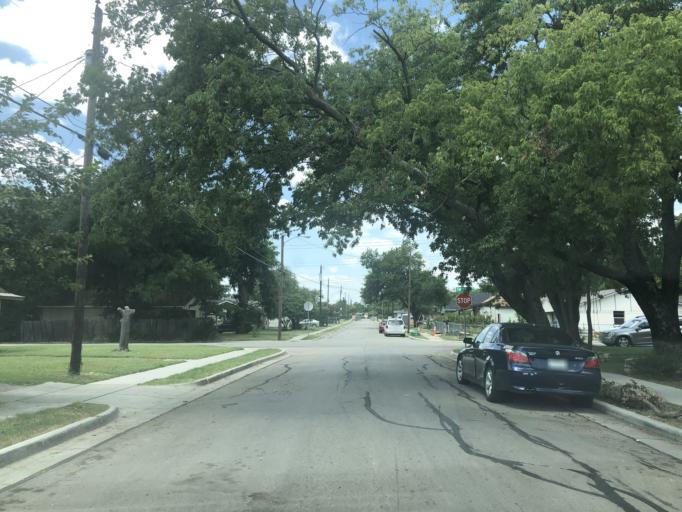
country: US
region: Texas
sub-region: Dallas County
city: Grand Prairie
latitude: 32.7340
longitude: -97.0323
